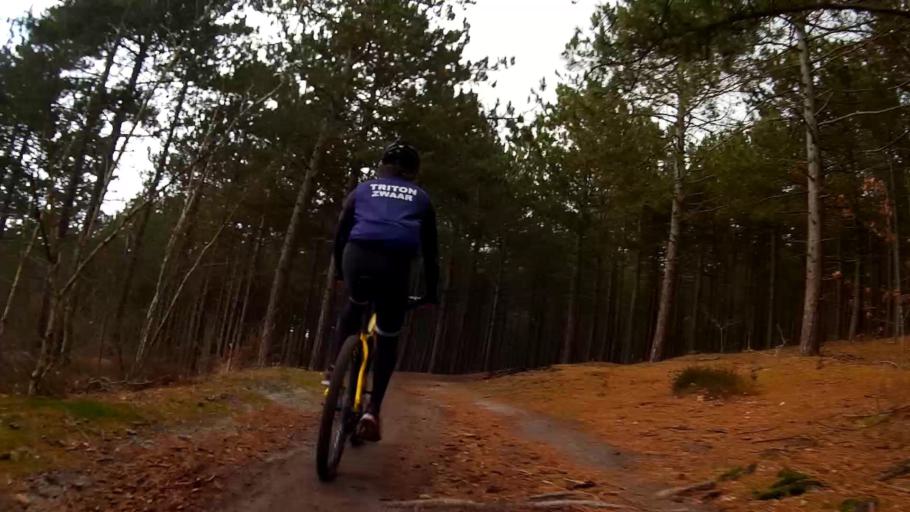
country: NL
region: North Holland
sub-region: Gemeente Bergen
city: Egmond aan Zee
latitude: 52.6895
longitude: 4.6680
